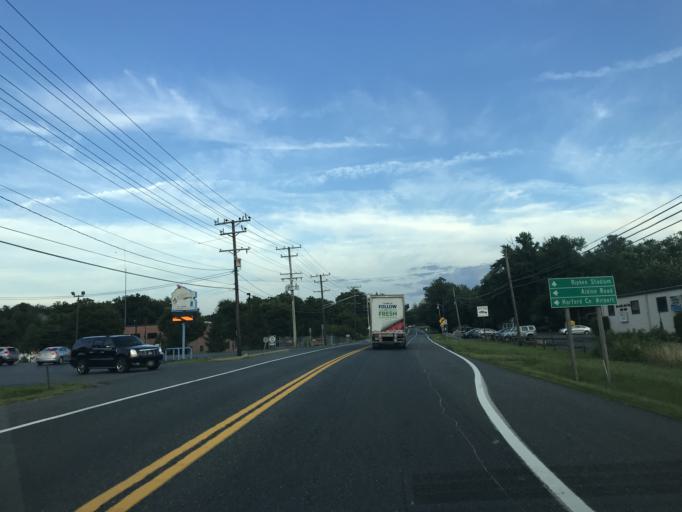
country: US
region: Maryland
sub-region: Harford County
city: Riverside
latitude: 39.5559
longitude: -76.2403
